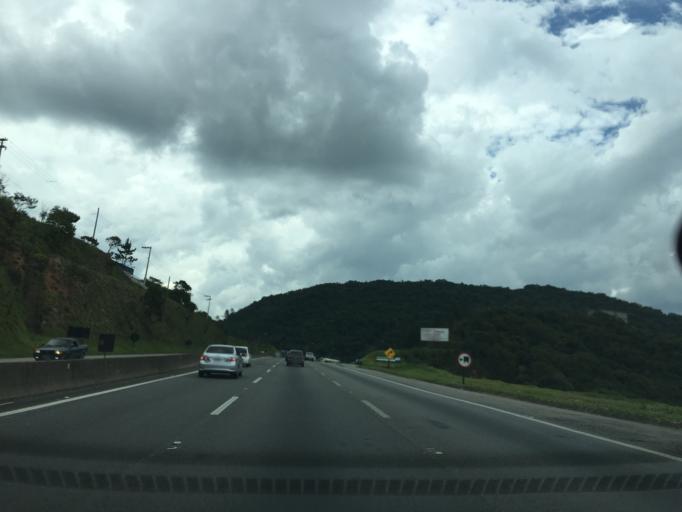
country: BR
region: Sao Paulo
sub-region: Mairipora
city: Mairipora
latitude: -23.2890
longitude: -46.5877
